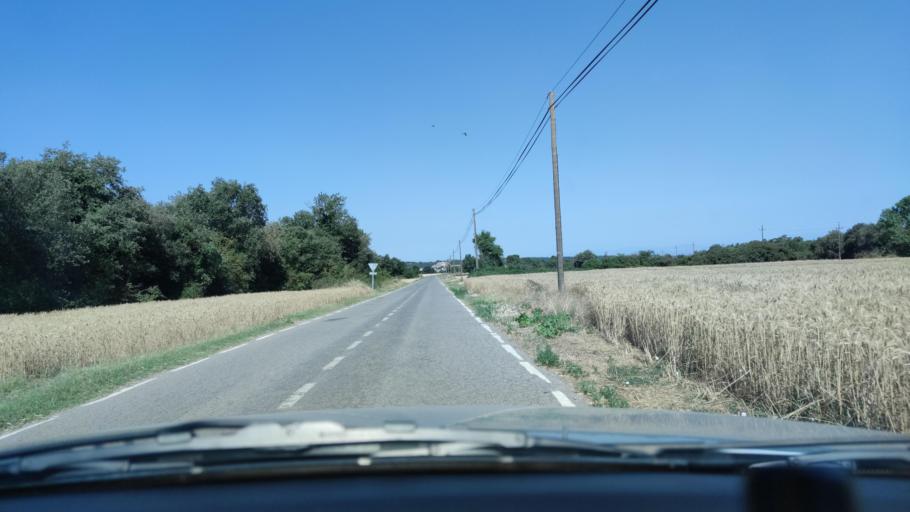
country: ES
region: Catalonia
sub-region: Provincia de Lleida
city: Sant Guim de Freixenet
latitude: 41.6438
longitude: 1.4144
